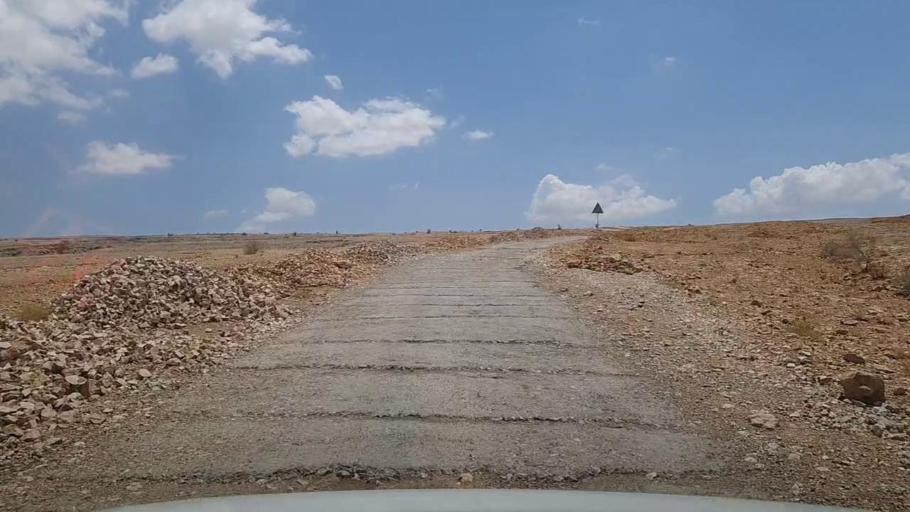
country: PK
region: Sindh
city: Bhan
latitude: 26.2889
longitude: 67.5795
